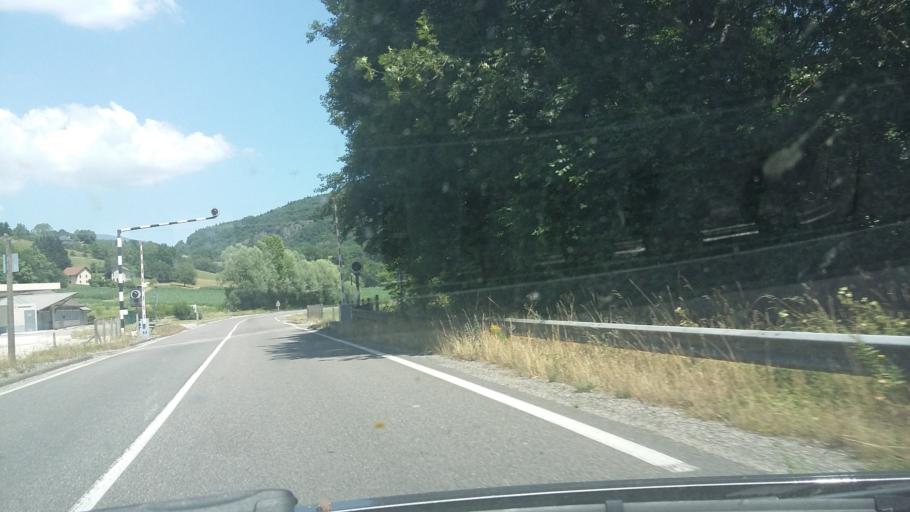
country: FR
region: Rhone-Alpes
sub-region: Departement de l'Ain
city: Belley
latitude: 45.7759
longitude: 5.6985
